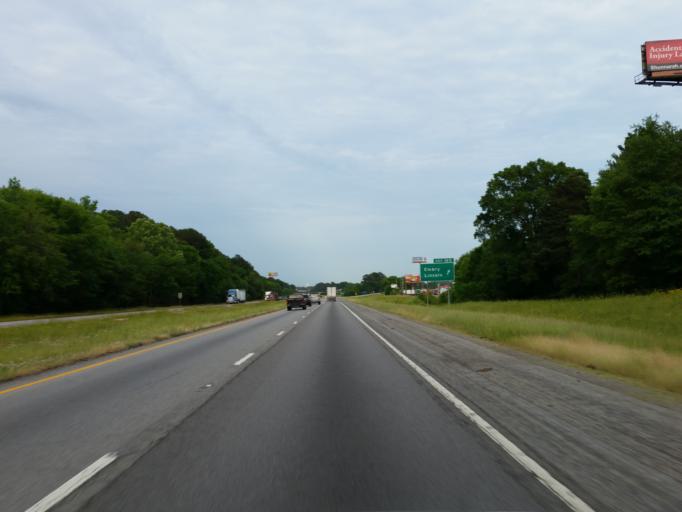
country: US
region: Alabama
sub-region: Saint Clair County
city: Riverside
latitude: 33.5924
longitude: -86.1711
